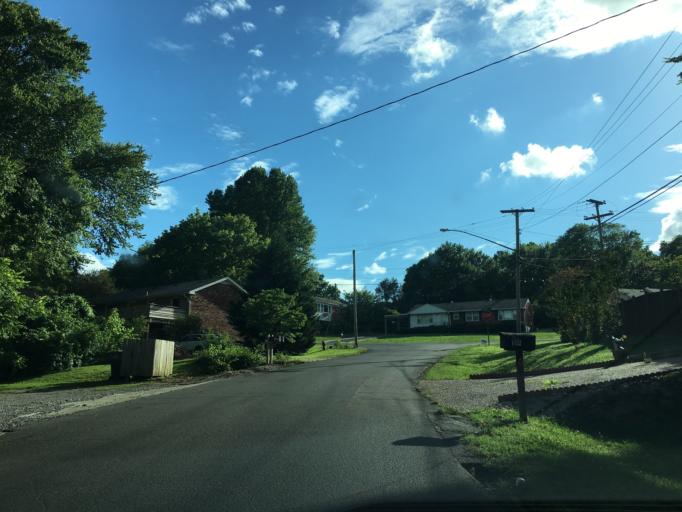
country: US
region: Tennessee
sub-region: Davidson County
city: Oak Hill
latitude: 36.0958
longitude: -86.7282
